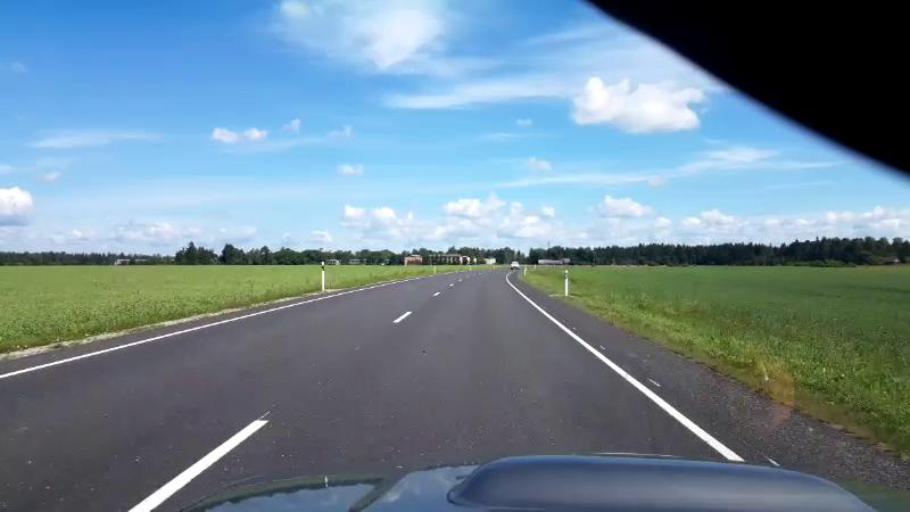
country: EE
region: Jaervamaa
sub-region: Jaerva-Jaani vald
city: Jarva-Jaani
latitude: 59.1211
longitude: 25.7365
